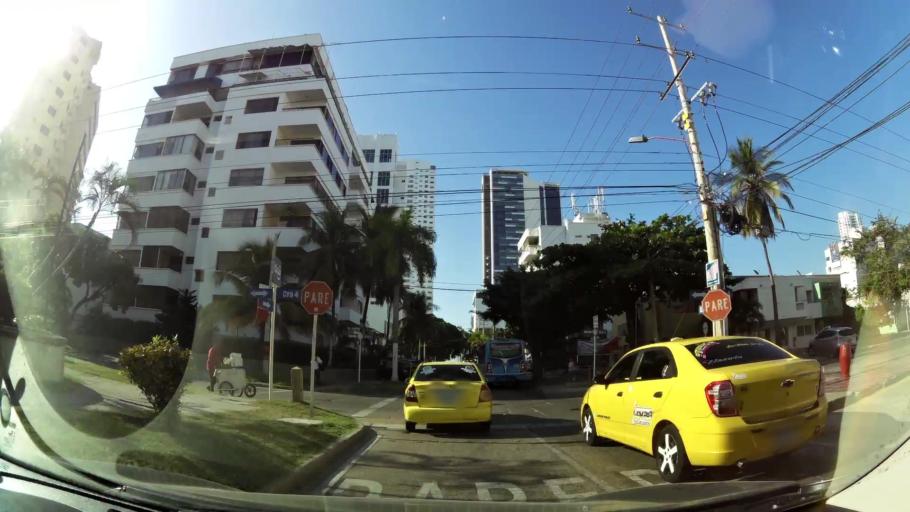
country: CO
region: Bolivar
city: Cartagena
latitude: 10.3980
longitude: -75.5579
